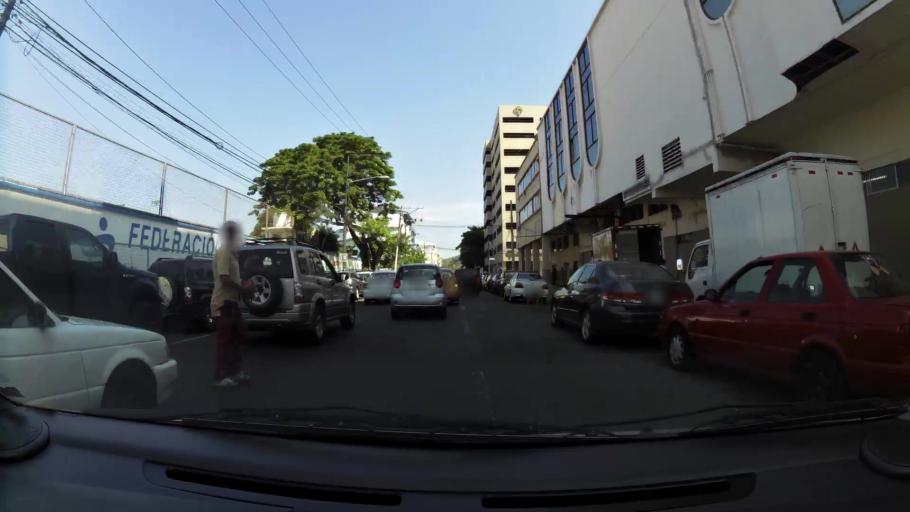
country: EC
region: Guayas
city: Guayaquil
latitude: -2.1894
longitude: -79.8917
